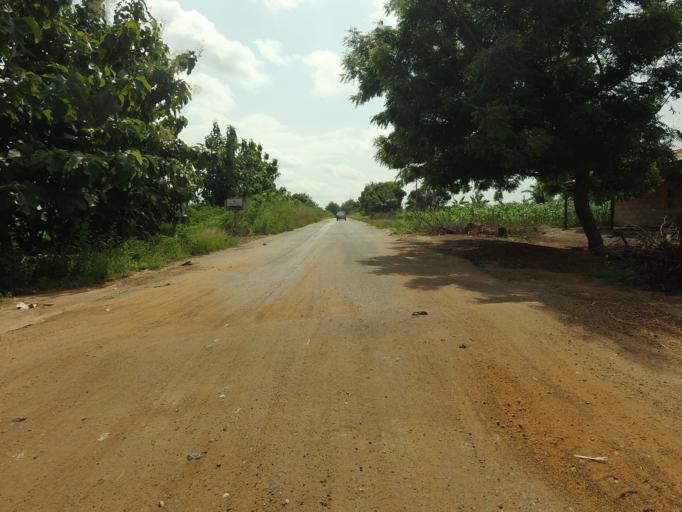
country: TG
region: Maritime
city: Lome
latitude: 6.2642
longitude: 0.9543
